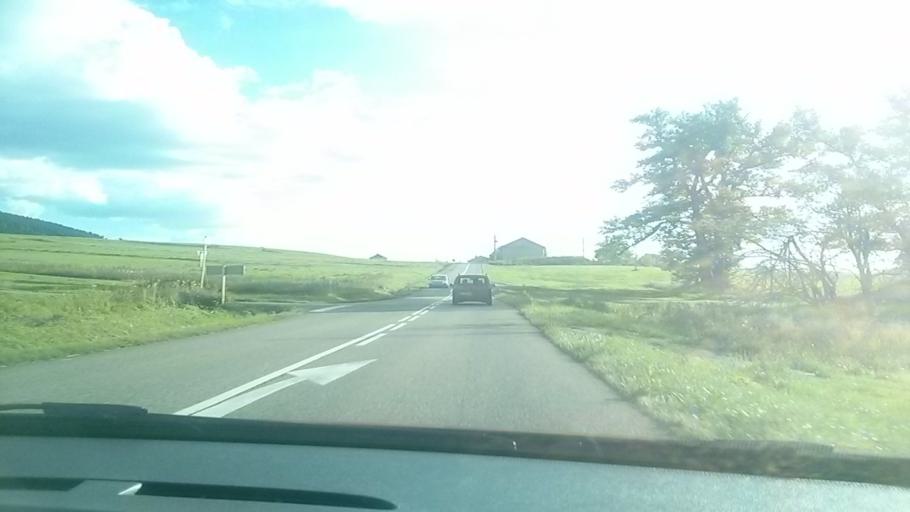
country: FR
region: Franche-Comte
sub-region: Departement du Jura
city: Les Rousses
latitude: 46.5076
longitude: 6.1073
